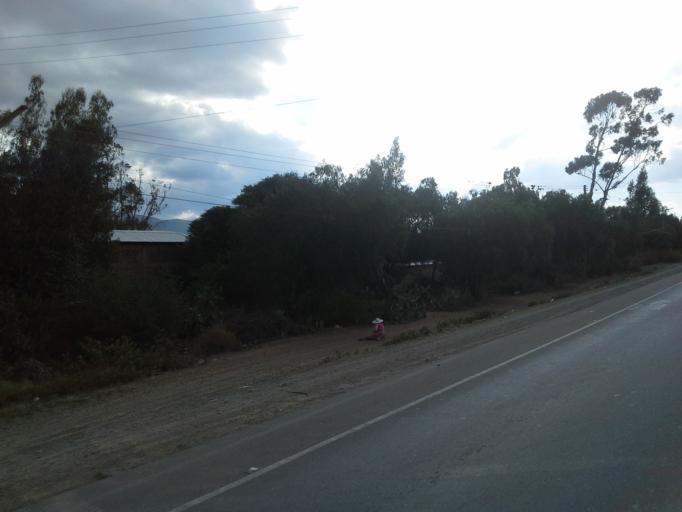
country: BO
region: Cochabamba
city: Tarata
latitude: -17.5437
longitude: -66.0433
